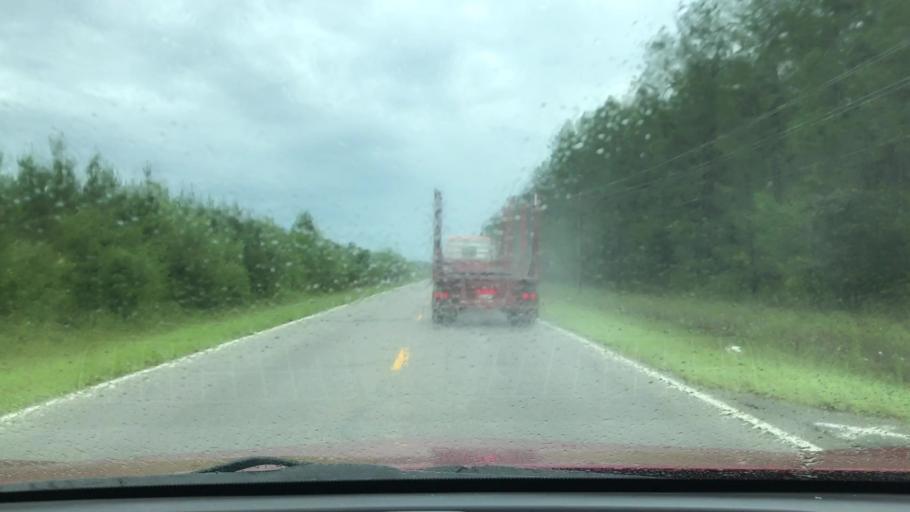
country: US
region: South Carolina
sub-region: Georgetown County
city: Georgetown
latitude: 33.5114
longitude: -79.2515
